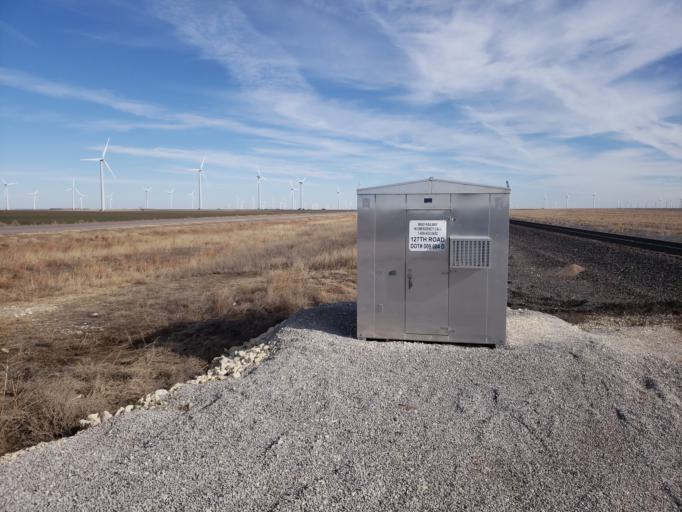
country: US
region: Kansas
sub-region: Hodgeman County
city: Jetmore
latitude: 37.8586
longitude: -99.7349
